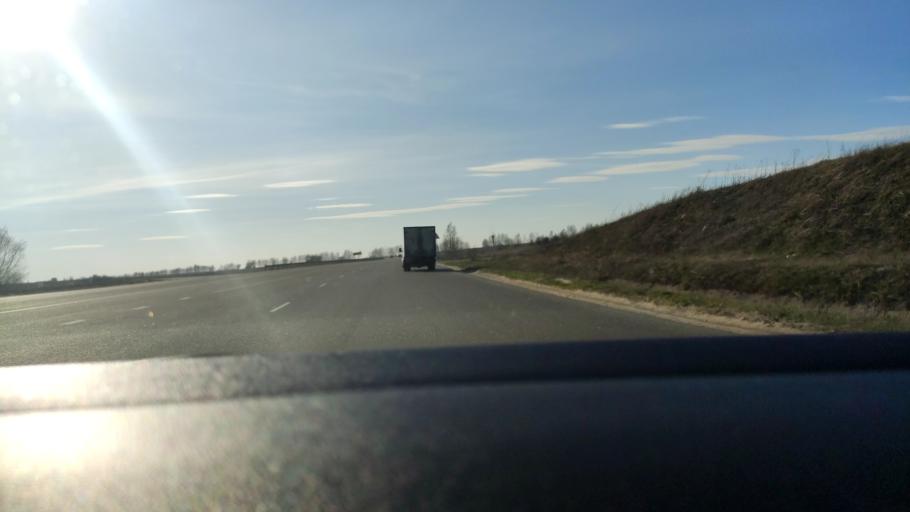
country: RU
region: Voronezj
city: Kolodeznyy
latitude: 51.3282
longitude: 39.1467
